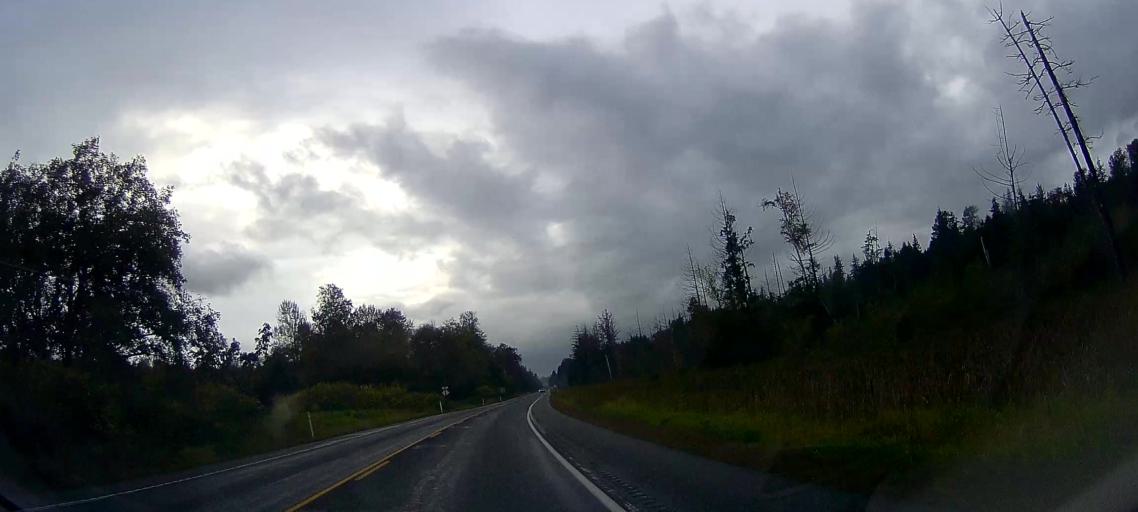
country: US
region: Washington
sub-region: Skagit County
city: Sedro-Woolley
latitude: 48.5290
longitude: -122.1602
